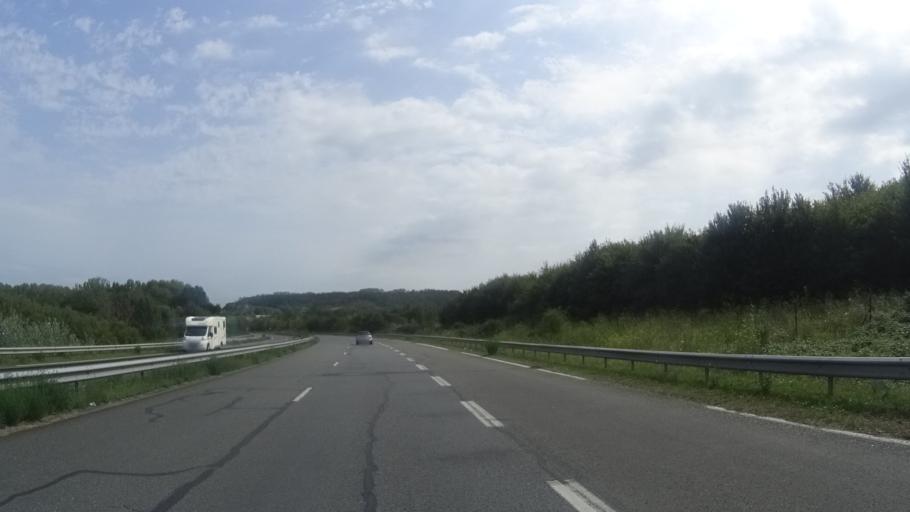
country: FR
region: Aquitaine
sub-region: Departement de la Dordogne
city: Neuvic
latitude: 45.0843
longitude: 0.4653
